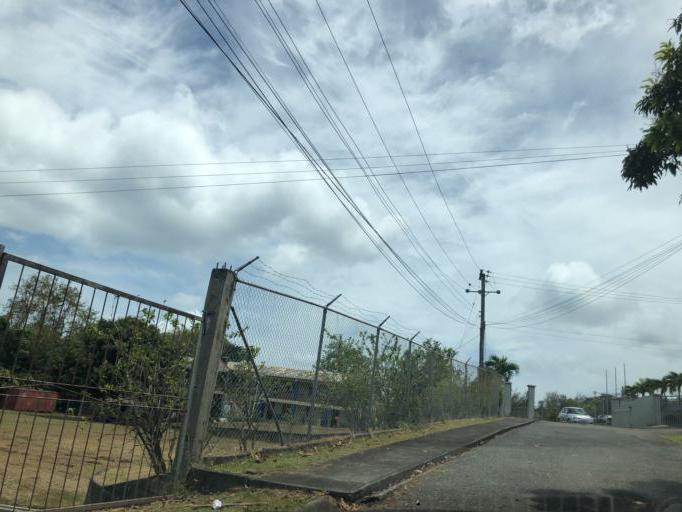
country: LC
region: Castries Quarter
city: Castries
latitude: 13.9935
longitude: -61.0090
